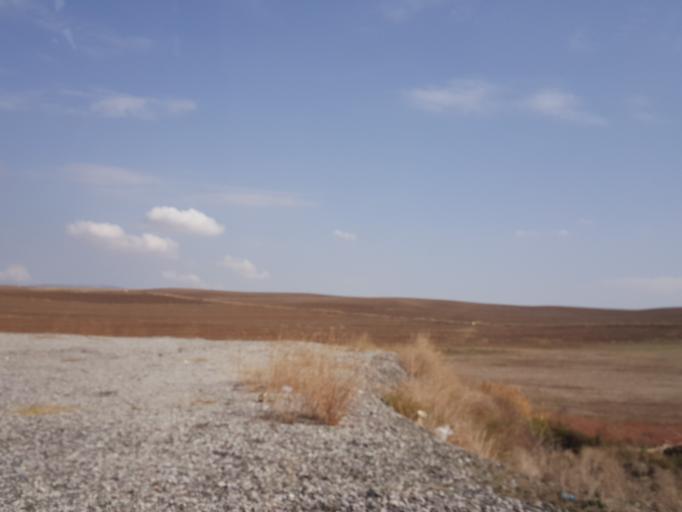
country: TR
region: Corum
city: Alaca
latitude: 40.1574
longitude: 34.8731
